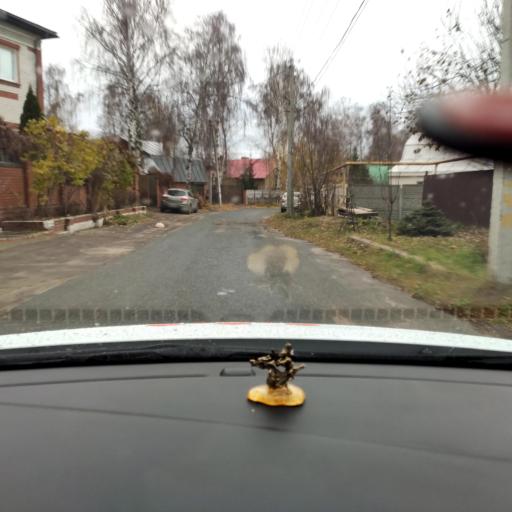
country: RU
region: Tatarstan
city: Vysokaya Gora
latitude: 55.8455
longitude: 49.2383
